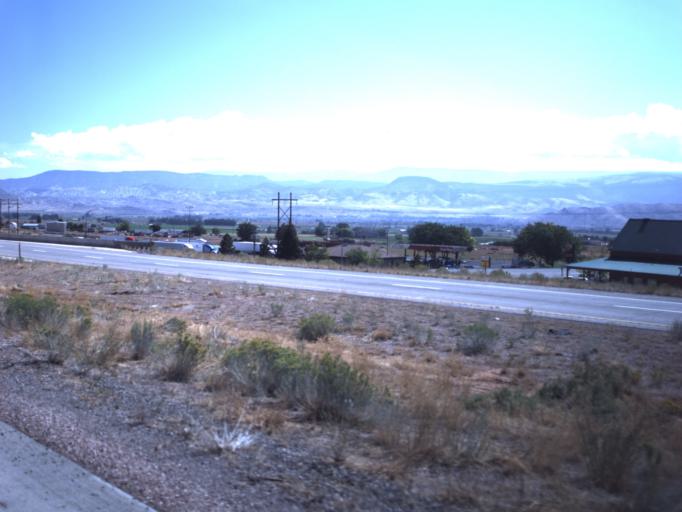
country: US
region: Utah
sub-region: Sevier County
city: Richfield
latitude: 38.7893
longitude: -112.0850
